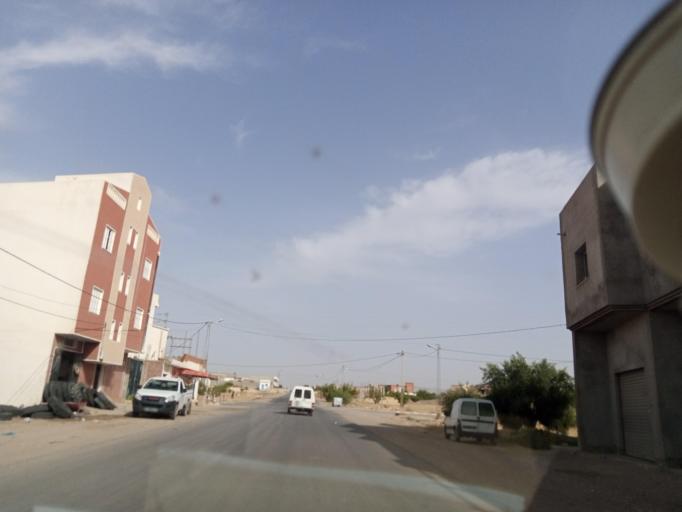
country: TN
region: Al Qasrayn
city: Kasserine
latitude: 35.2152
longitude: 8.8995
